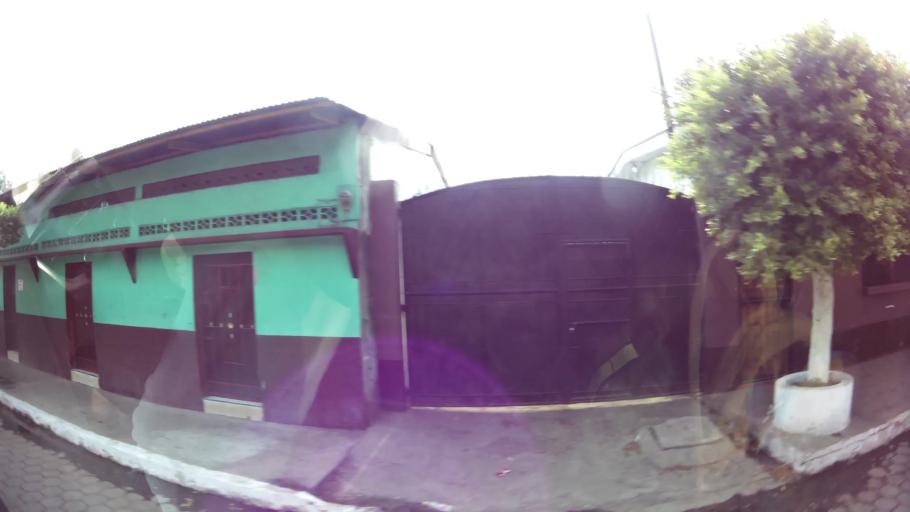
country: NI
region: Chinandega
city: Chinandega
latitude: 12.6228
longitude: -87.1306
